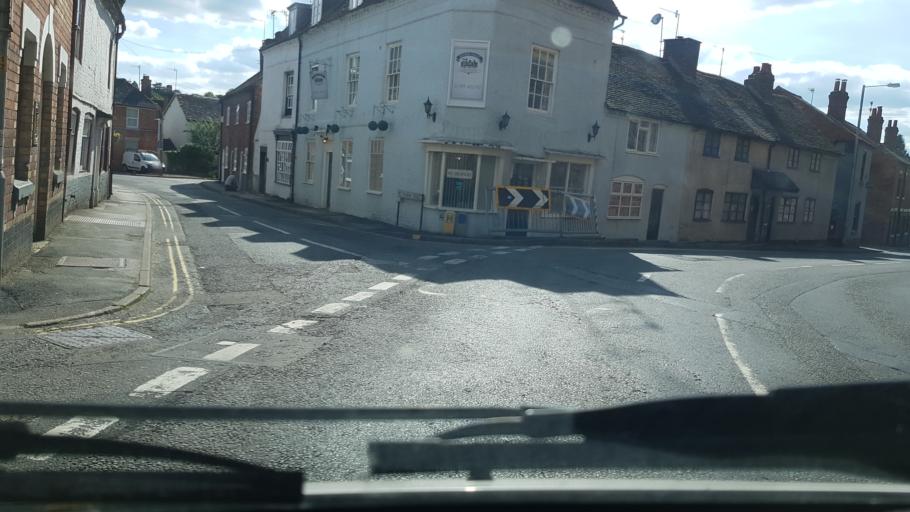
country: GB
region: England
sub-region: Worcestershire
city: Bewdley
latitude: 52.3767
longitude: -2.3090
